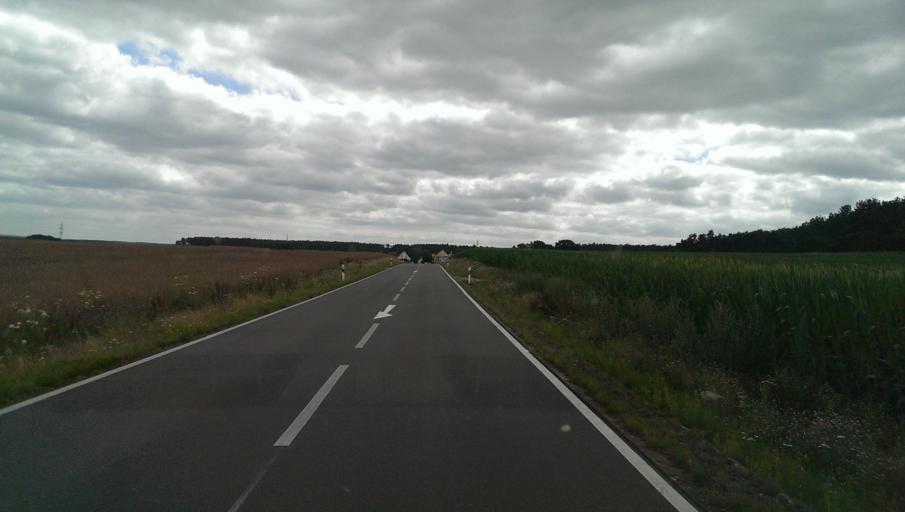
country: DE
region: Brandenburg
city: Belzig
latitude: 52.1051
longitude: 12.6196
